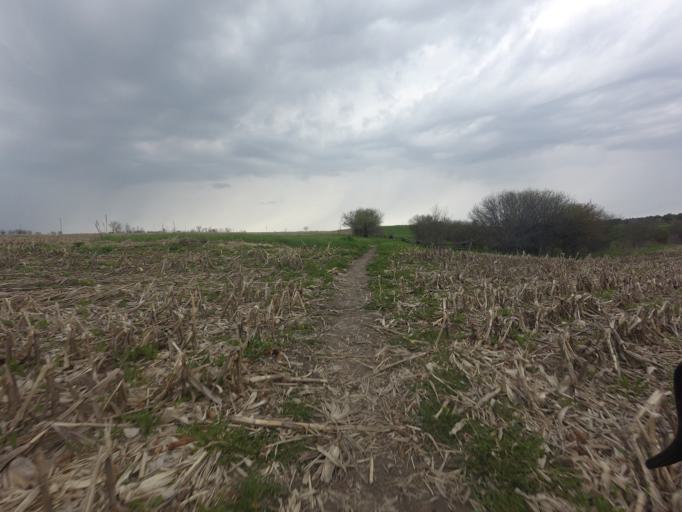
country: CA
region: Ontario
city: Carleton Place
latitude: 45.2261
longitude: -76.2086
